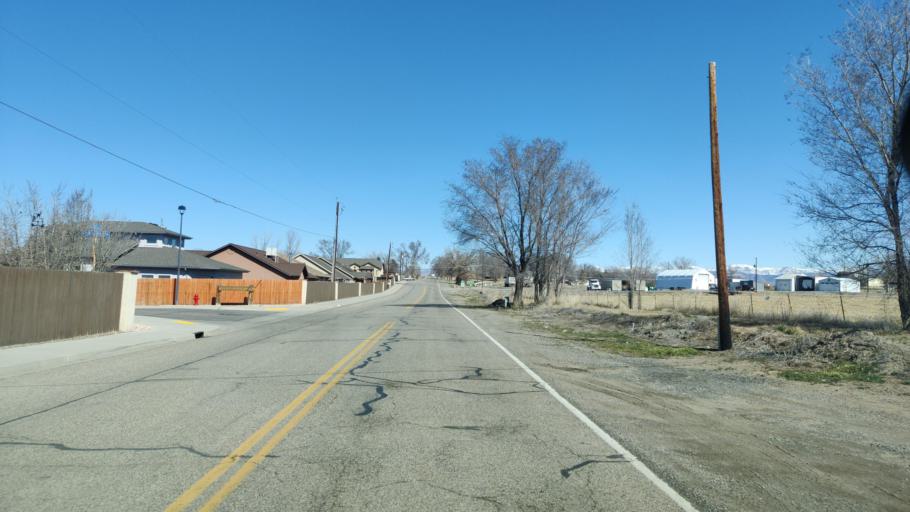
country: US
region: Colorado
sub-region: Mesa County
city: Fruita
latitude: 39.1762
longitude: -108.7197
